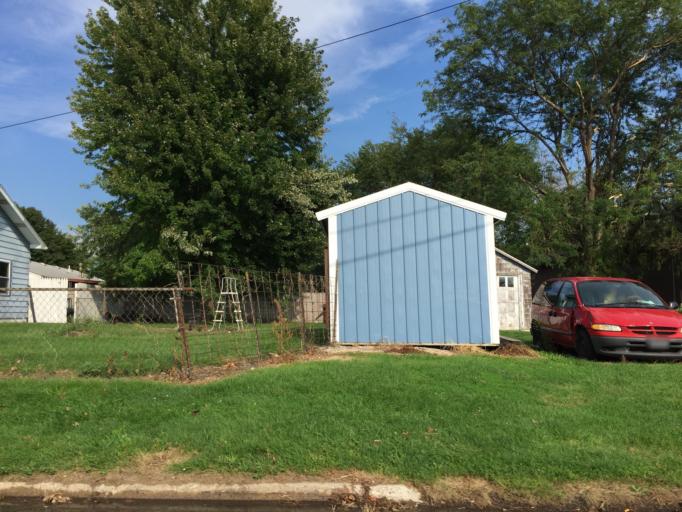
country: US
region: Indiana
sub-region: Howard County
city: Kokomo
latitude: 40.4693
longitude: -86.1159
